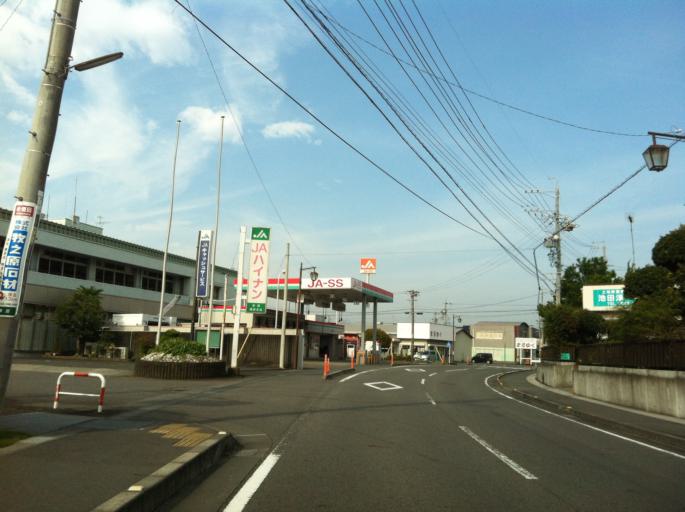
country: JP
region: Shizuoka
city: Sagara
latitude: 34.7444
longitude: 138.2224
